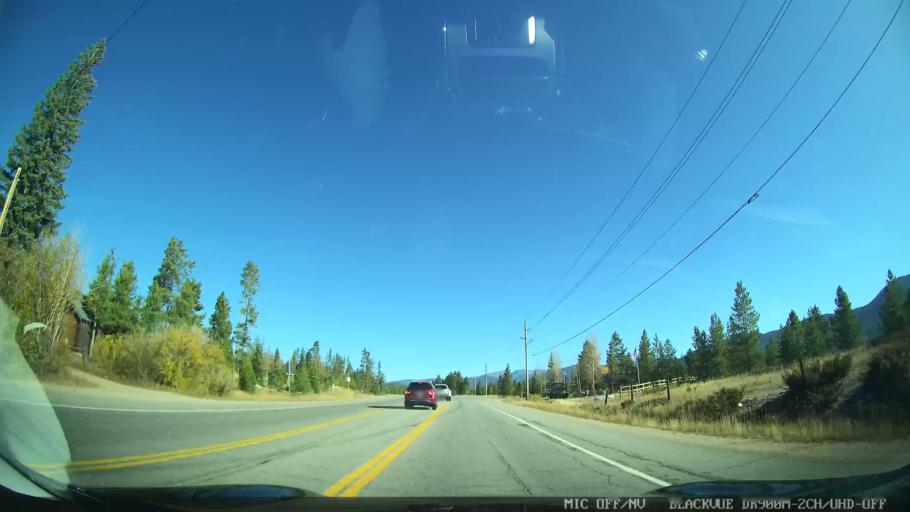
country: US
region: Colorado
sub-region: Grand County
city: Granby
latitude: 40.2051
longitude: -105.8608
